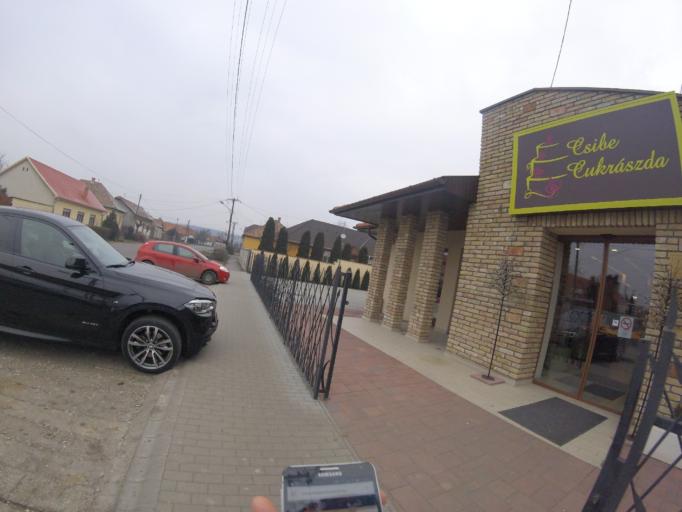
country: HU
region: Nograd
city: Paszto
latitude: 47.9216
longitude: 19.6917
